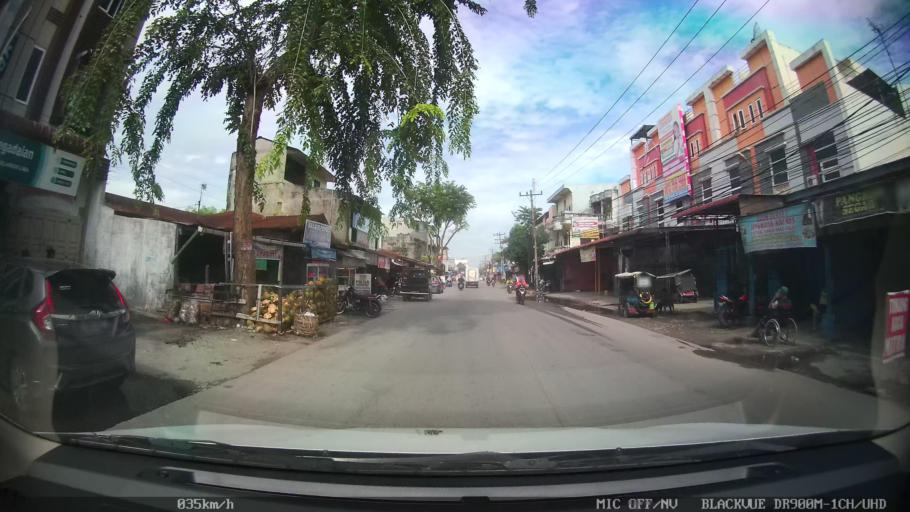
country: ID
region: North Sumatra
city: Sunggal
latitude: 3.6086
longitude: 98.6115
